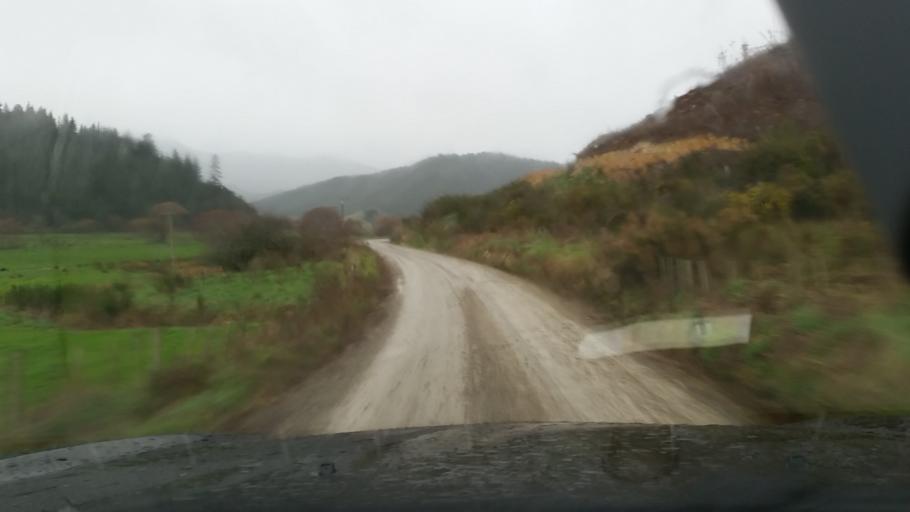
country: NZ
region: Marlborough
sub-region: Marlborough District
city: Picton
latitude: -41.3438
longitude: 173.9281
